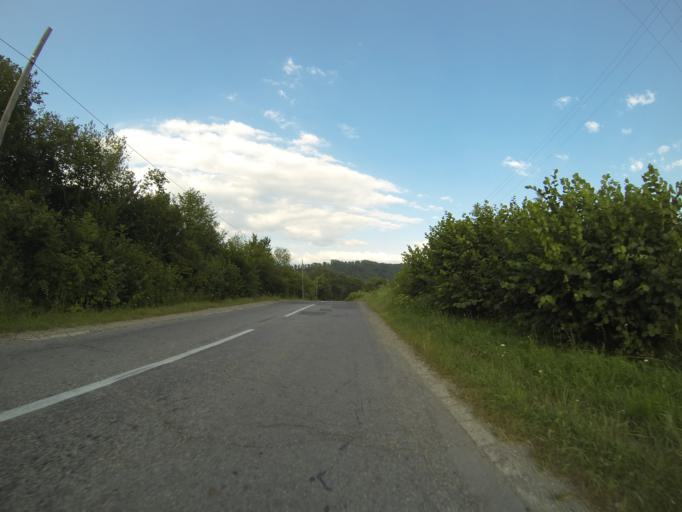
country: RO
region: Brasov
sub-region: Comuna Sinca Veche
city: Persani
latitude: 45.7428
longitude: 25.2094
